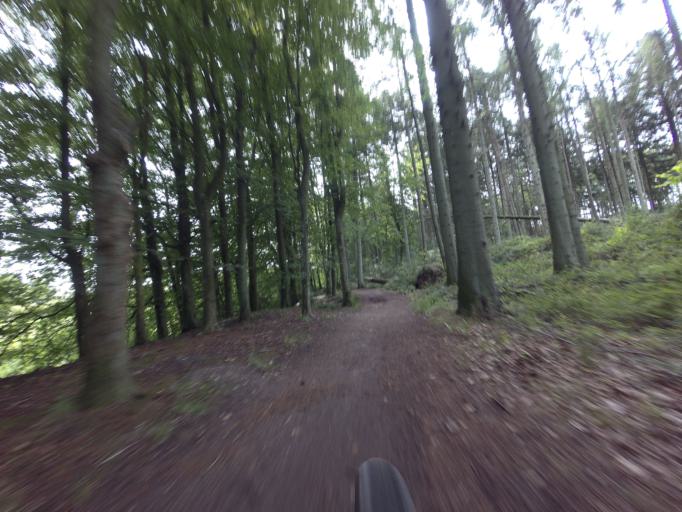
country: DK
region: North Denmark
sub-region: Hjorring Kommune
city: Sindal
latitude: 57.5849
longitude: 10.1797
